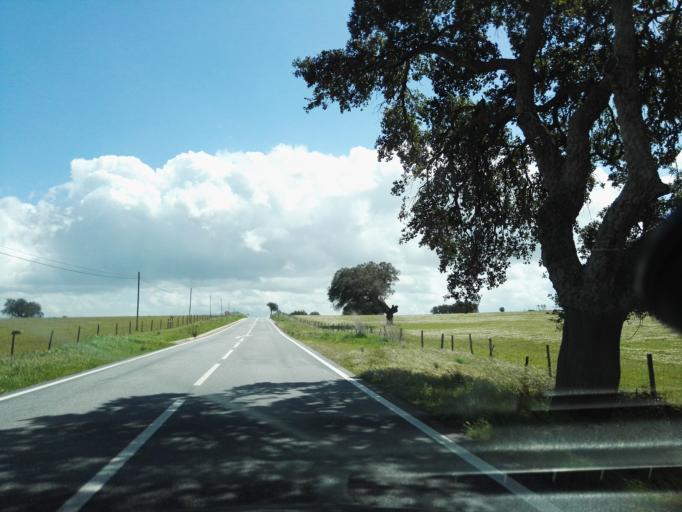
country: PT
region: Portalegre
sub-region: Arronches
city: Arronches
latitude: 39.1204
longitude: -7.2670
